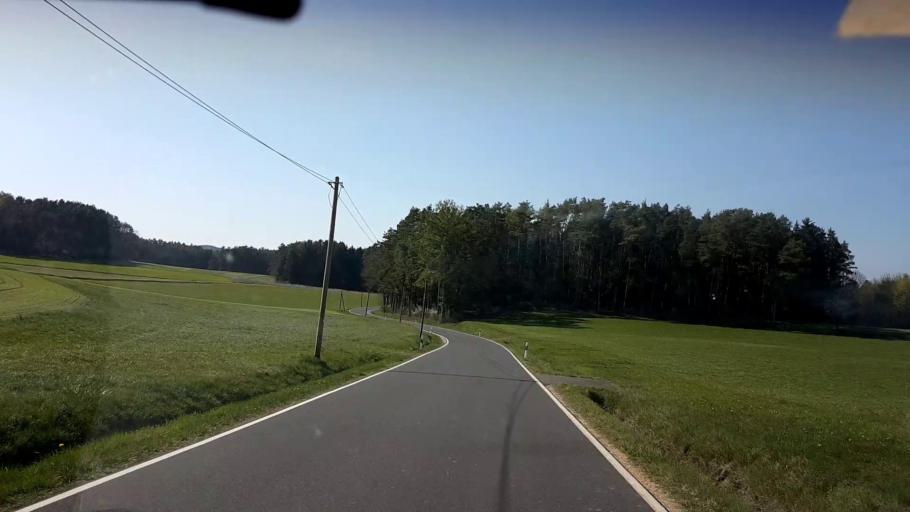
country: DE
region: Bavaria
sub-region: Upper Franconia
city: Pottenstein
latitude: 49.7917
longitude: 11.3828
